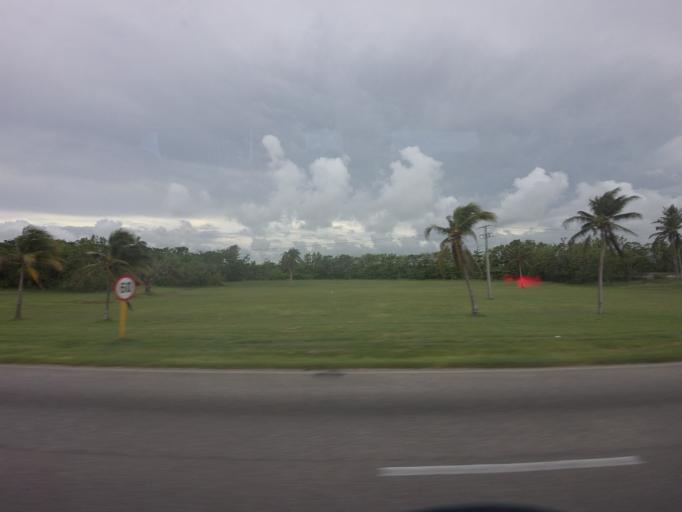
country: CU
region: Matanzas
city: Varadero
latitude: 23.1286
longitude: -81.3131
